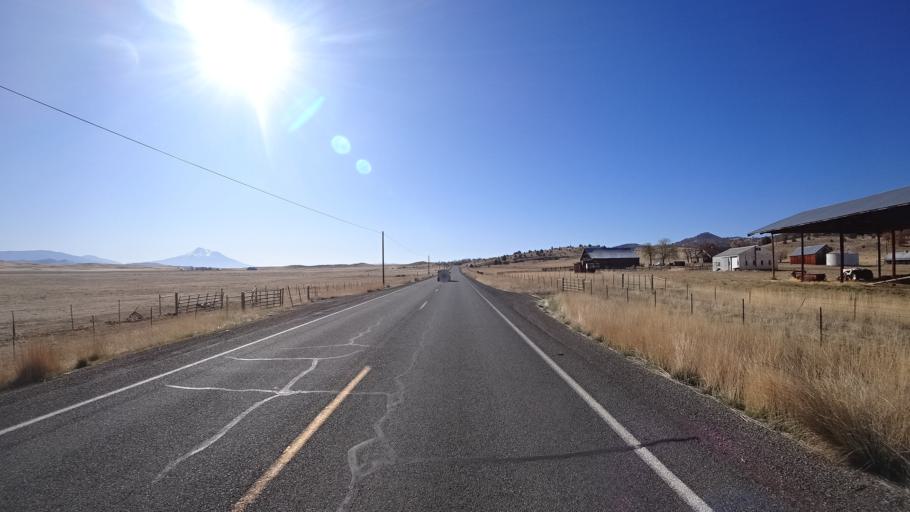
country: US
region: California
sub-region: Siskiyou County
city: Montague
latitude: 41.8265
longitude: -122.4941
